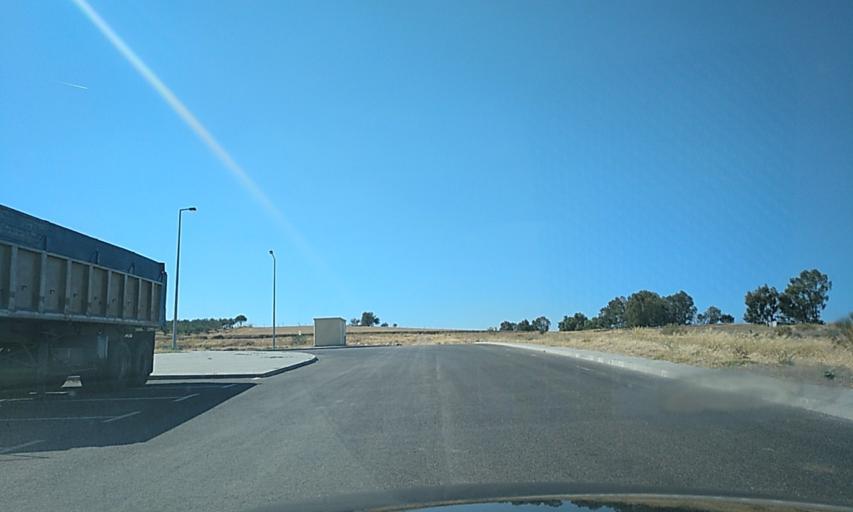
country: PT
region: Portalegre
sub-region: Campo Maior
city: Campo Maior
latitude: 39.0260
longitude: -7.0604
